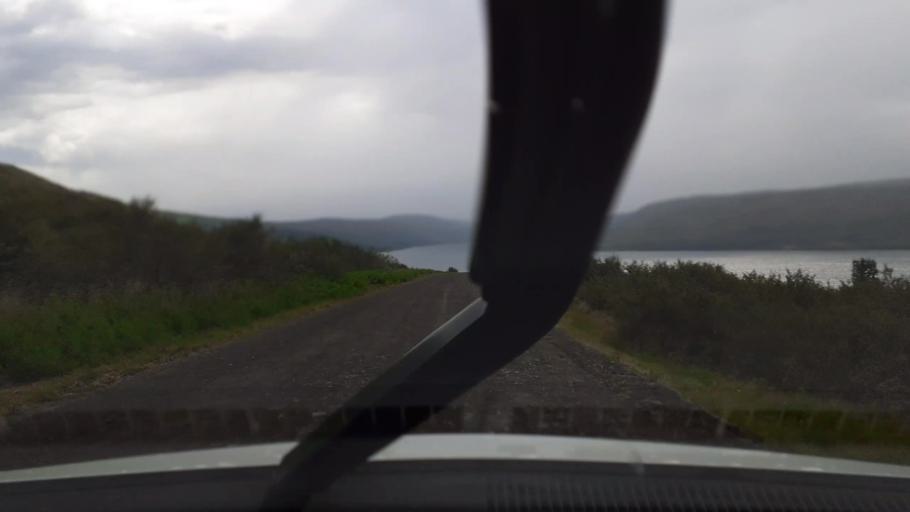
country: IS
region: Capital Region
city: Mosfellsbaer
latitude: 64.5254
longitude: -21.4799
